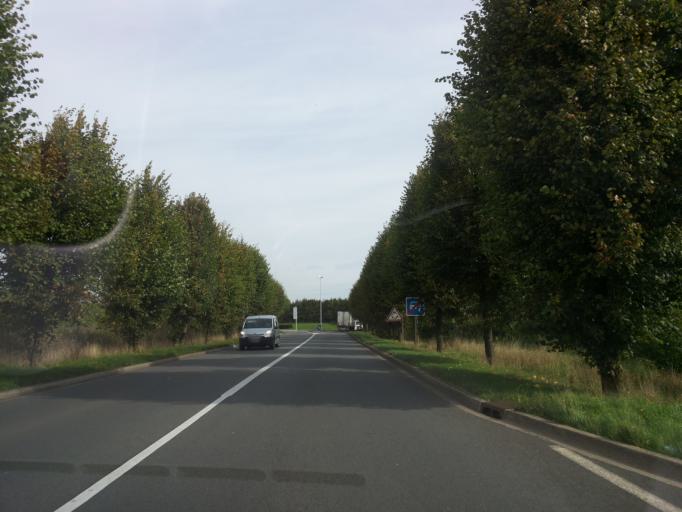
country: FR
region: Nord-Pas-de-Calais
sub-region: Departement du Nord
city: Raillencourt-Sainte-Olle
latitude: 50.1838
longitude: 3.1879
